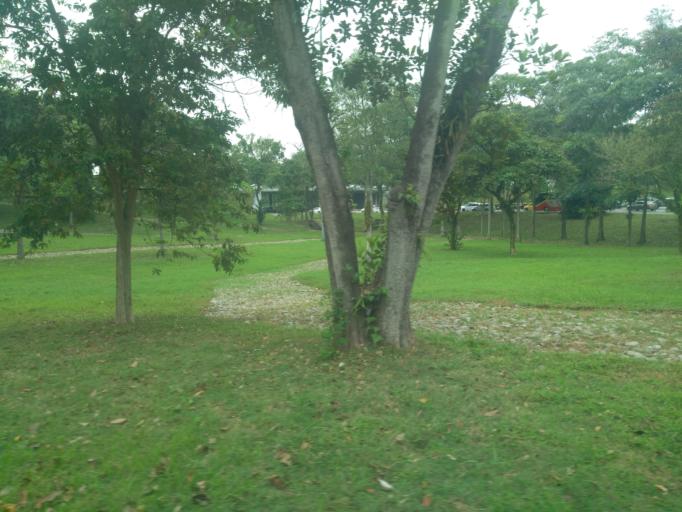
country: MY
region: Johor
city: Johor Bahru
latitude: 1.4879
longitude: 103.7412
